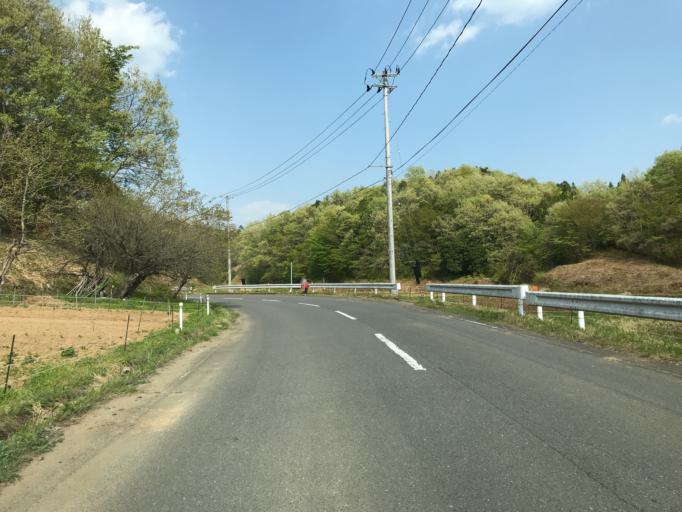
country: JP
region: Fukushima
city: Iwaki
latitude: 36.9959
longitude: 140.7715
